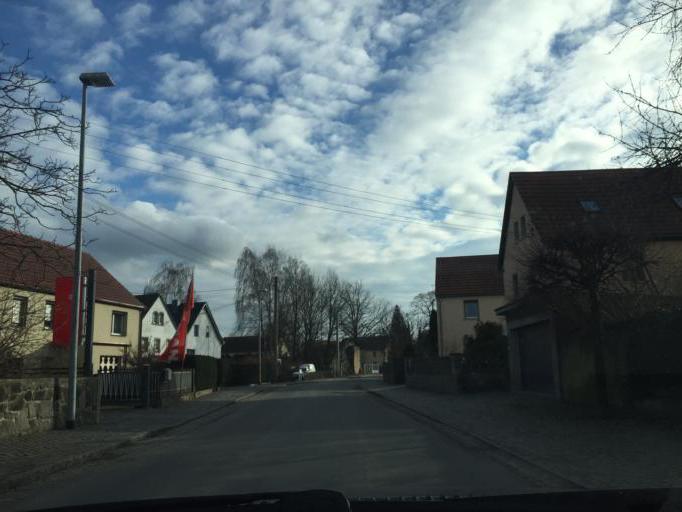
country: DE
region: Saxony
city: Ebersbach
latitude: 51.2409
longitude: 13.6605
